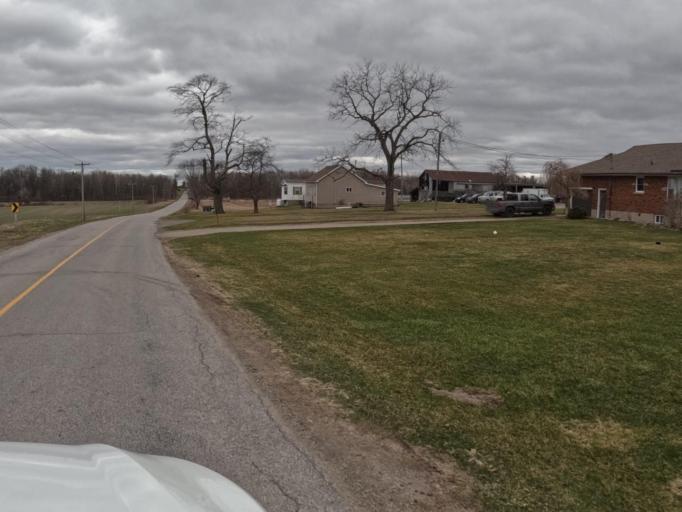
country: CA
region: Ontario
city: Norfolk County
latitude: 42.9567
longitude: -80.3948
